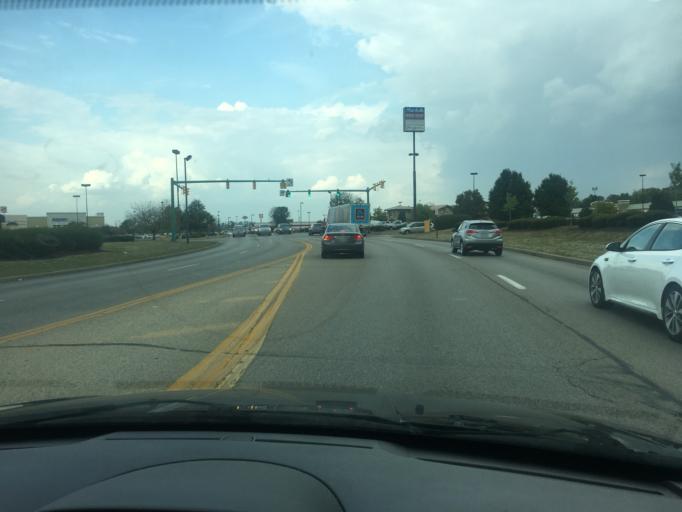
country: US
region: Ohio
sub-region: Clark County
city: Springfield
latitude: 39.9453
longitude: -83.8343
